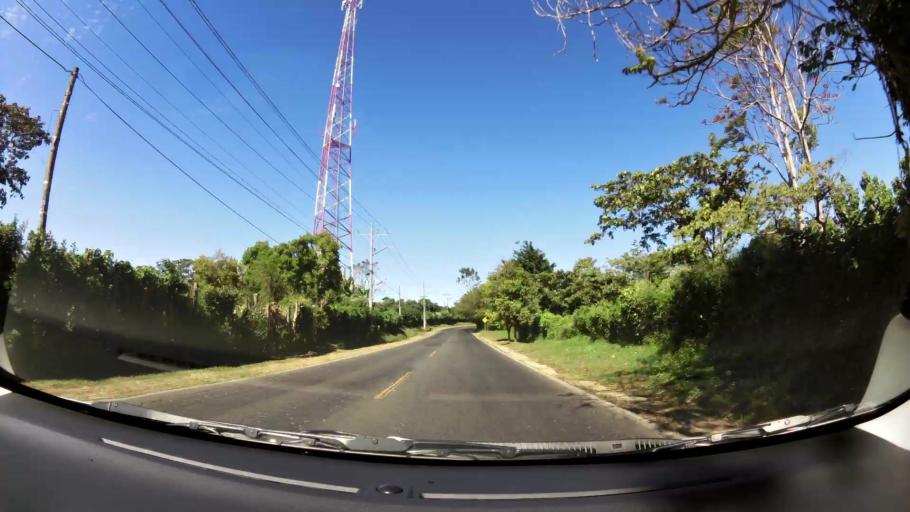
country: SV
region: Ahuachapan
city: Concepcion de Ataco
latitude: 13.8569
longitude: -89.8488
